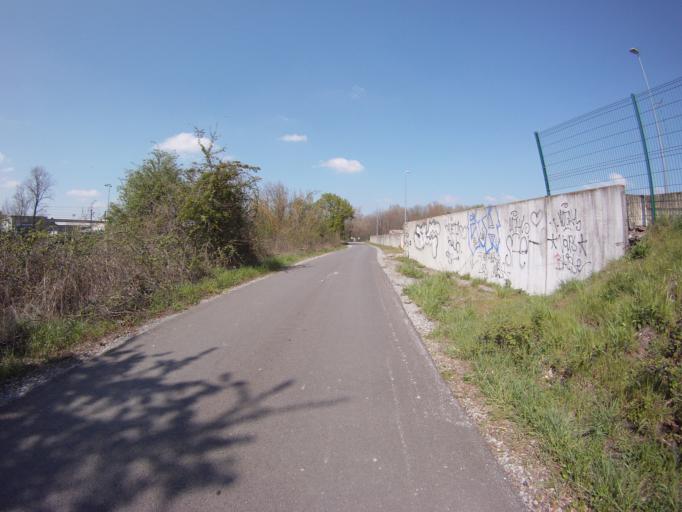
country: FR
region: Lorraine
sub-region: Departement de Meurthe-et-Moselle
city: Blenod-les-Pont-a-Mousson
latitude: 48.8887
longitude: 6.0587
